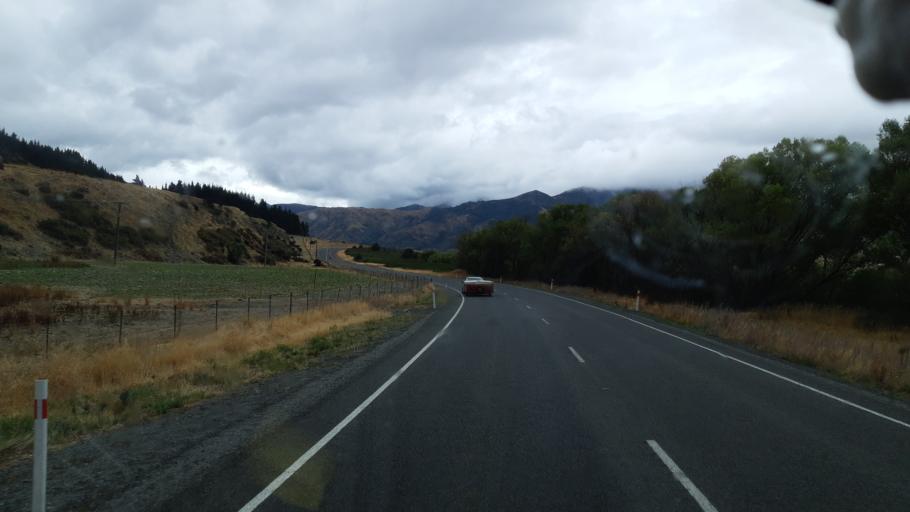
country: NZ
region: Canterbury
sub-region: Hurunui District
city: Amberley
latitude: -42.5736
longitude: 172.7182
